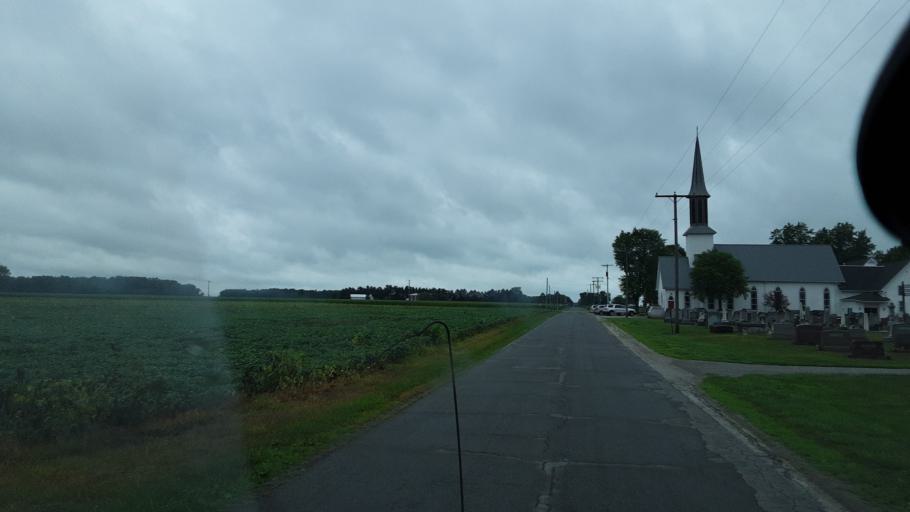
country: US
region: Ohio
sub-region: Van Wert County
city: Convoy
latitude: 40.8224
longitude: -84.7046
